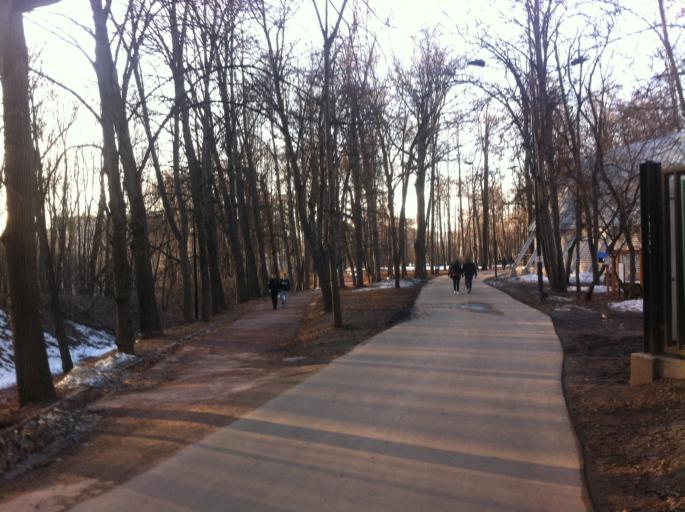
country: RU
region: Moscow
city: Novyye Cheremushki
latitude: 55.7177
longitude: 37.5906
